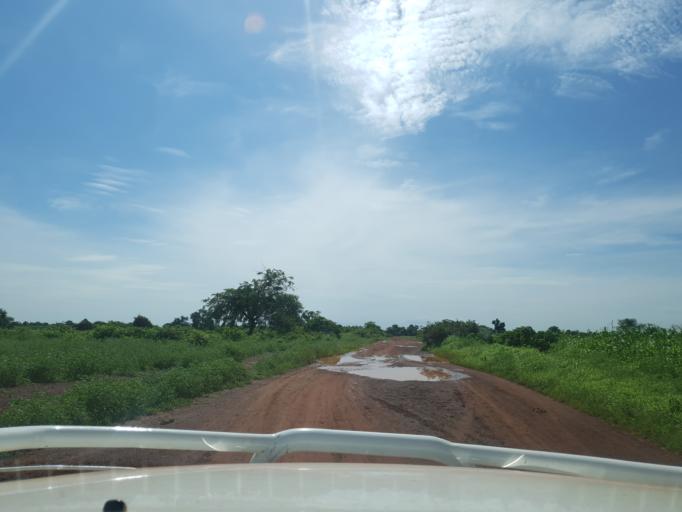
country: ML
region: Koulikoro
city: Banamba
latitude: 13.2756
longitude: -7.5448
